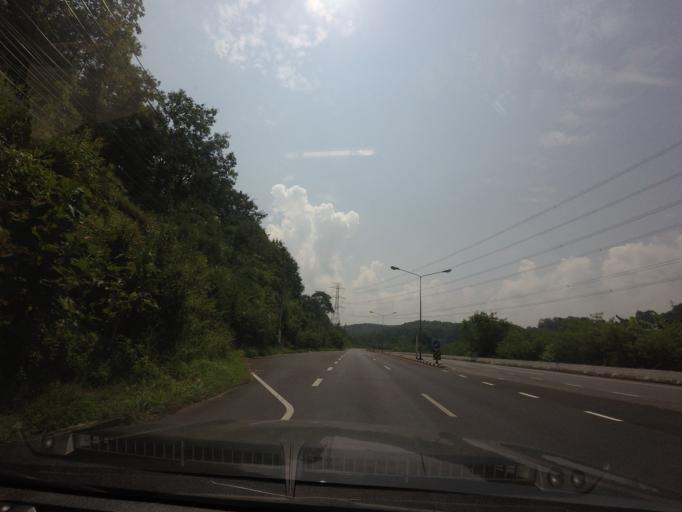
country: TH
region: Phrae
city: Den Chai
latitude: 17.8894
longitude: 100.0489
